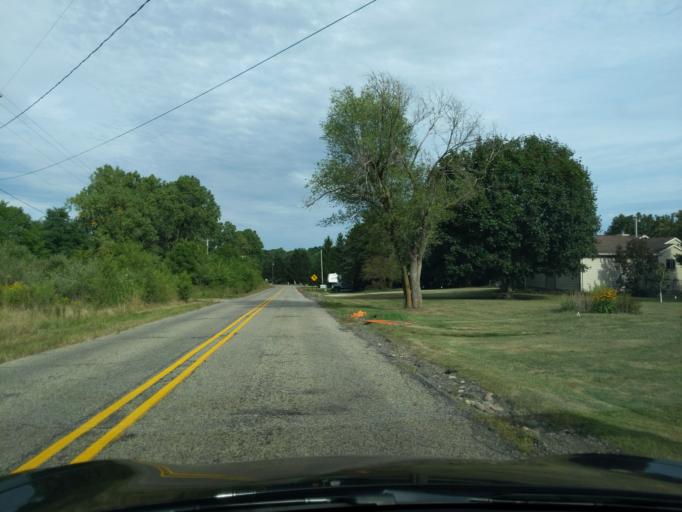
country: US
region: Michigan
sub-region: Eaton County
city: Dimondale
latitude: 42.6692
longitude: -84.6504
